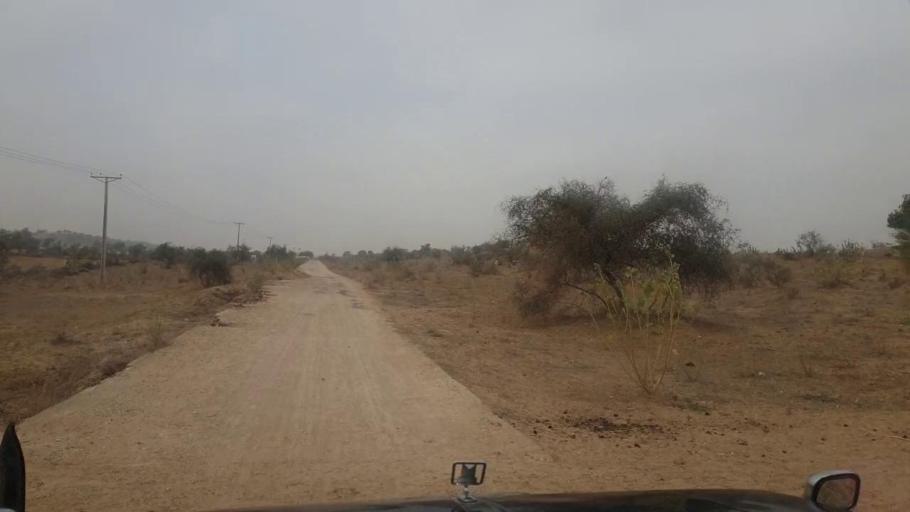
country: PK
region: Sindh
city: Umarkot
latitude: 25.1667
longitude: 70.0651
